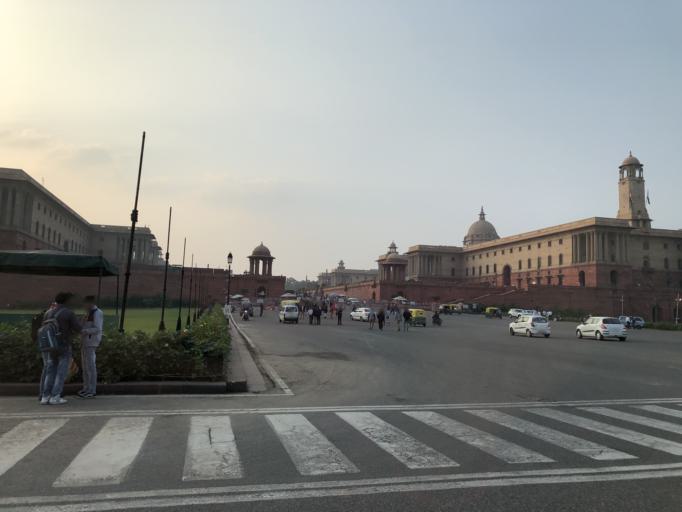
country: IN
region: NCT
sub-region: New Delhi
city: New Delhi
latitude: 28.6136
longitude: 77.2088
